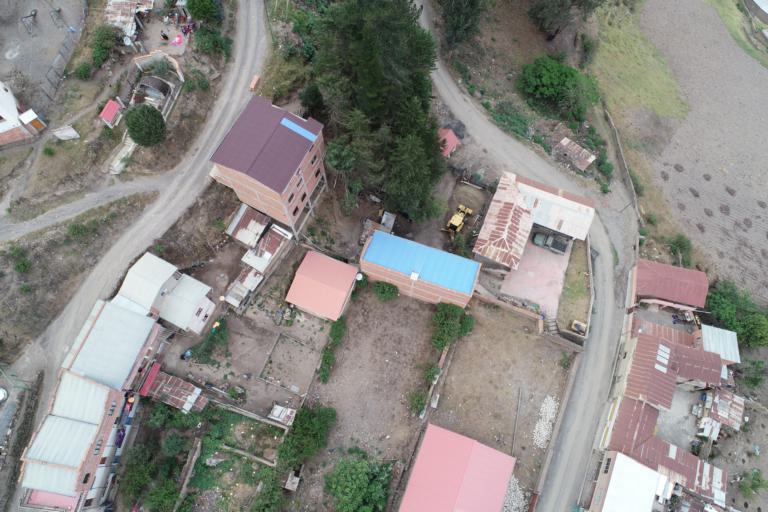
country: BO
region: La Paz
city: Sorata
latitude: -15.6370
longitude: -68.7037
